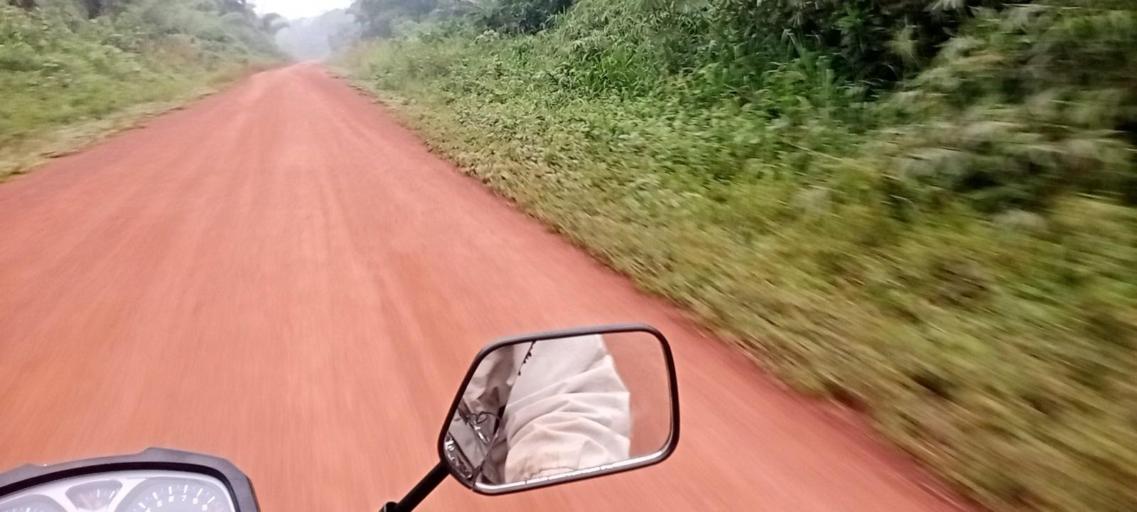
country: CD
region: Eastern Province
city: Kisangani
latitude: -0.0853
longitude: 25.6085
